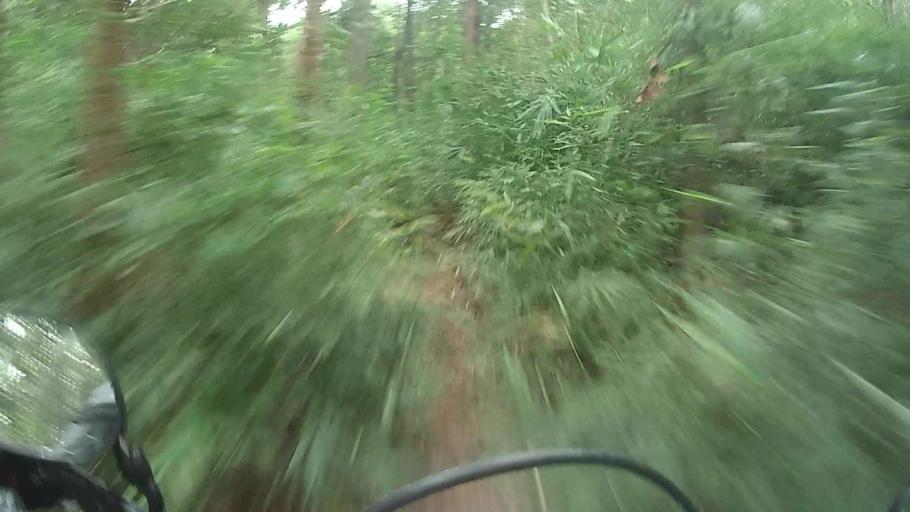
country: TH
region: Chiang Mai
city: Mae On
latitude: 18.7355
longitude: 99.2508
